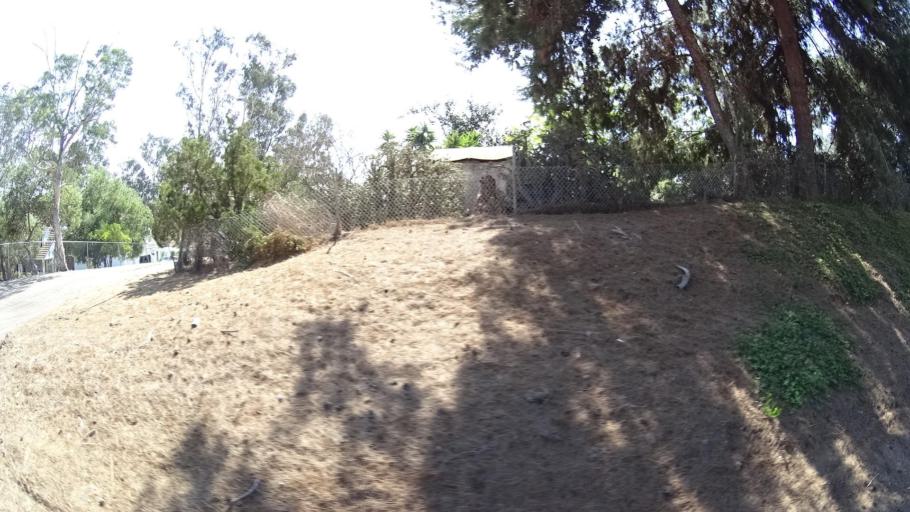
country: US
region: California
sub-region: San Diego County
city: La Presa
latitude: 32.6815
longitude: -116.9953
